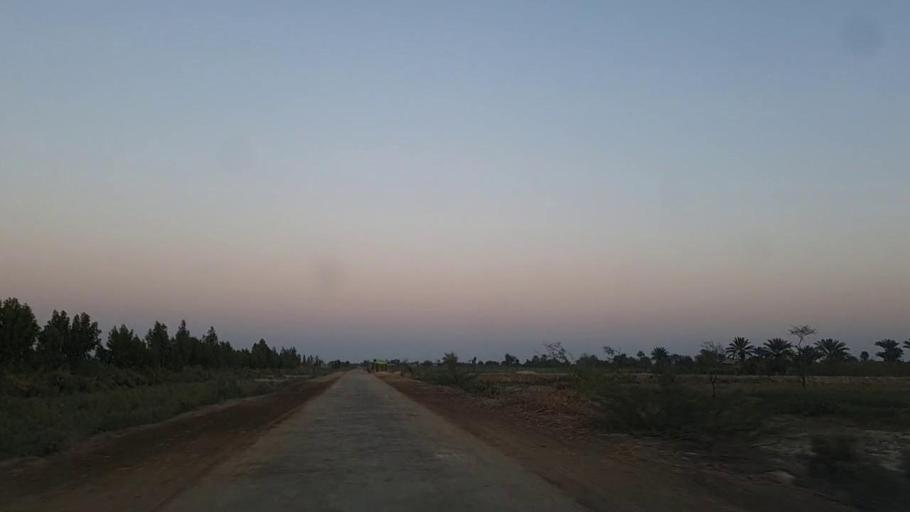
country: PK
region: Sindh
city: Samaro
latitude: 25.3252
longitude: 69.3970
